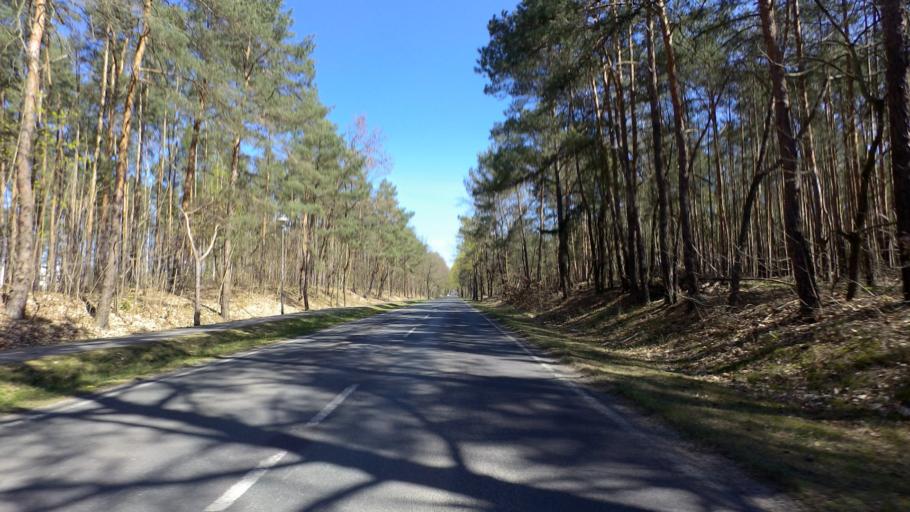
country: DE
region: Brandenburg
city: Zeuthen
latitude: 52.3432
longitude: 13.6183
